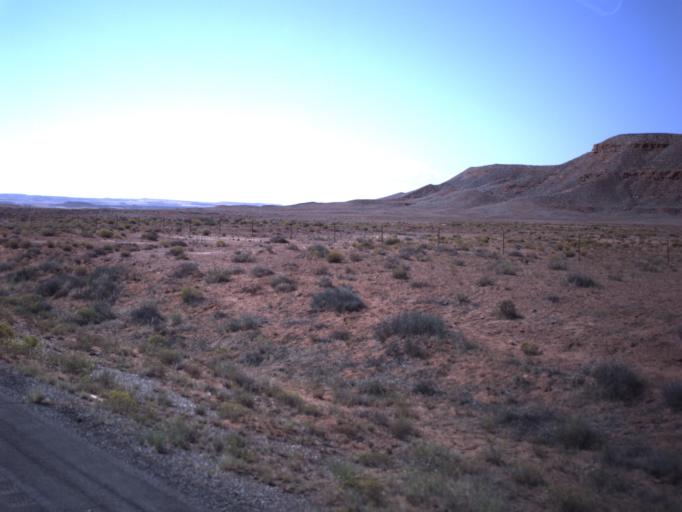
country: US
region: Utah
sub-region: San Juan County
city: Blanding
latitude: 37.0021
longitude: -109.6101
